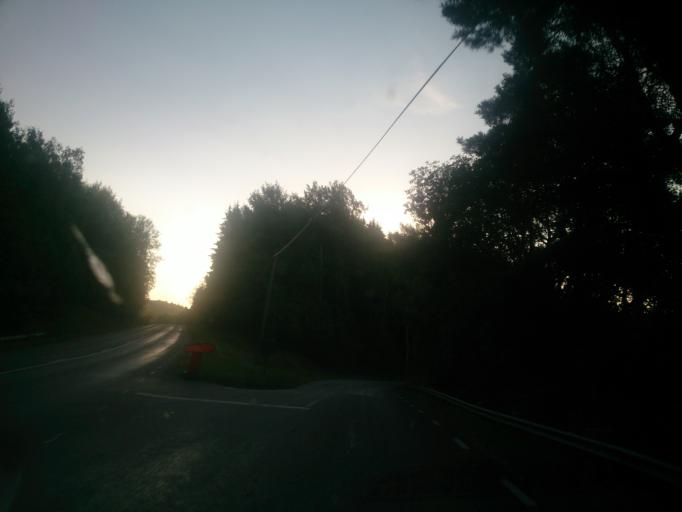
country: SE
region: Soedermanland
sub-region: Nykopings Kommun
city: Nykoping
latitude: 58.8686
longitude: 17.1663
